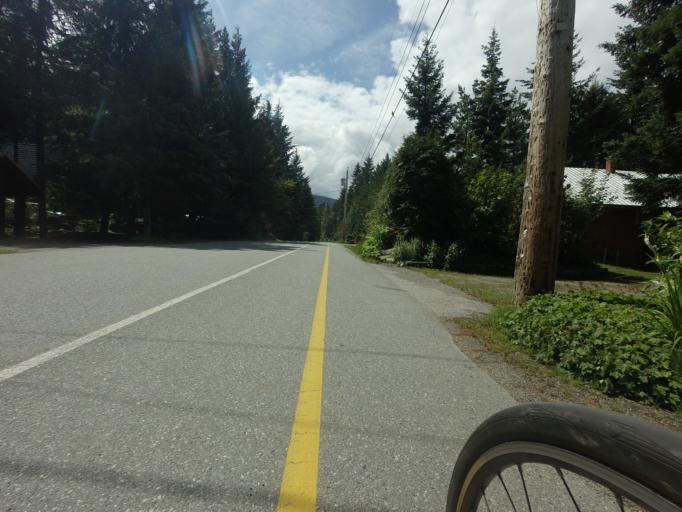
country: CA
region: British Columbia
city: Whistler
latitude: 50.1090
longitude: -122.9786
